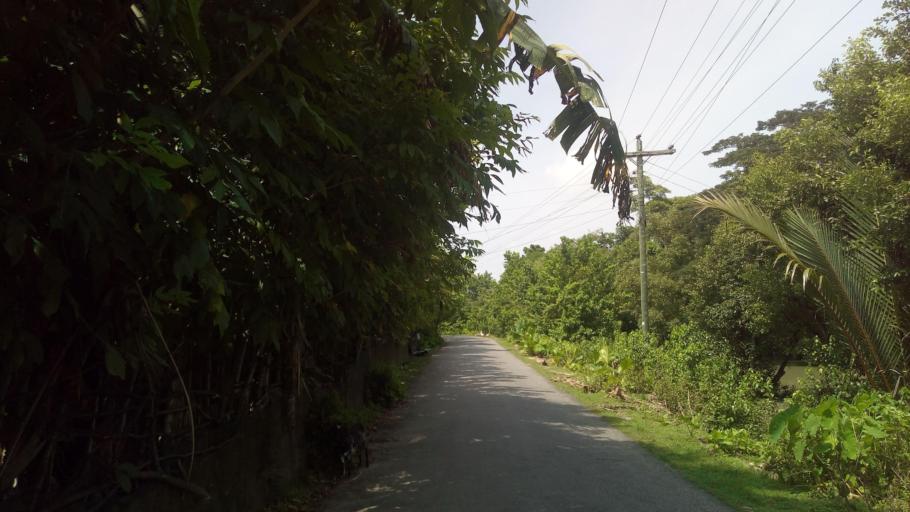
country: BD
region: Khulna
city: Phultala
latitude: 22.5779
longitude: 89.4538
